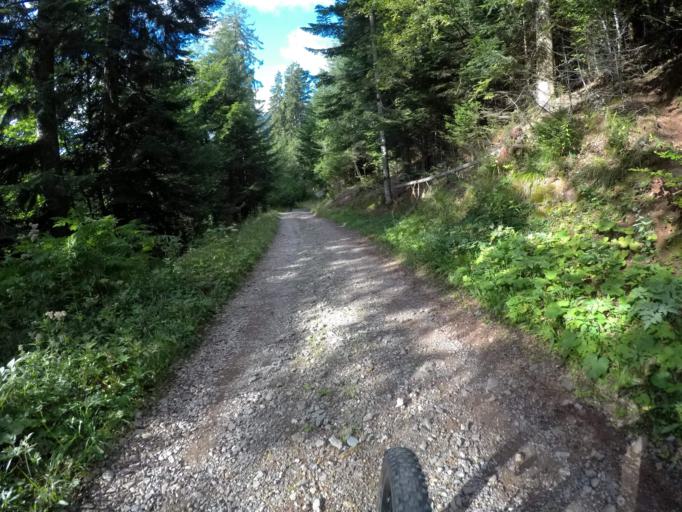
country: IT
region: Friuli Venezia Giulia
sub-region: Provincia di Udine
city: Paularo
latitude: 46.5415
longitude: 13.1038
